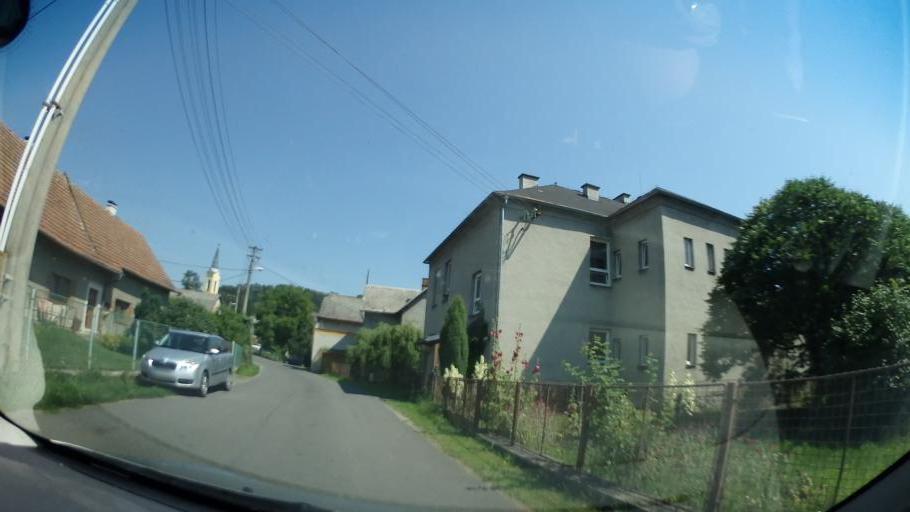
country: CZ
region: Olomoucky
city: Zabreh
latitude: 49.8655
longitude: 16.8179
